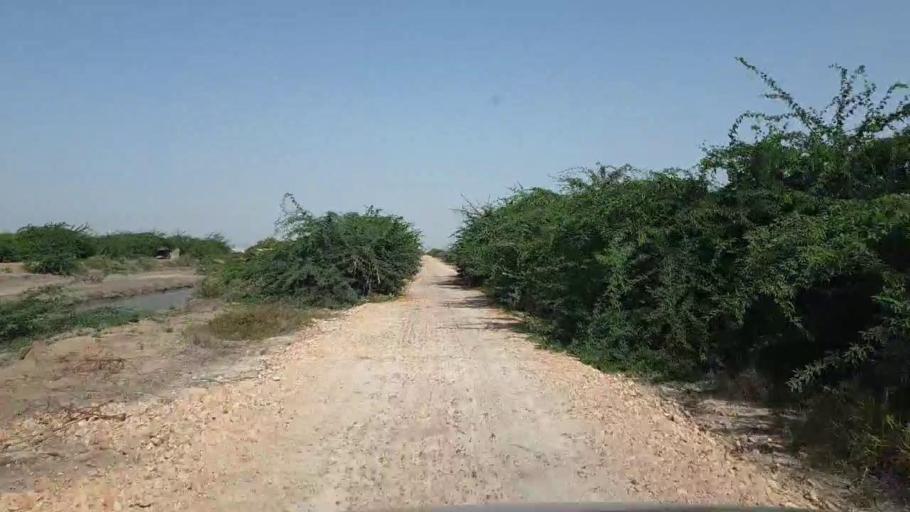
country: PK
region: Sindh
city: Tando Bago
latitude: 24.7294
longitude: 69.0739
